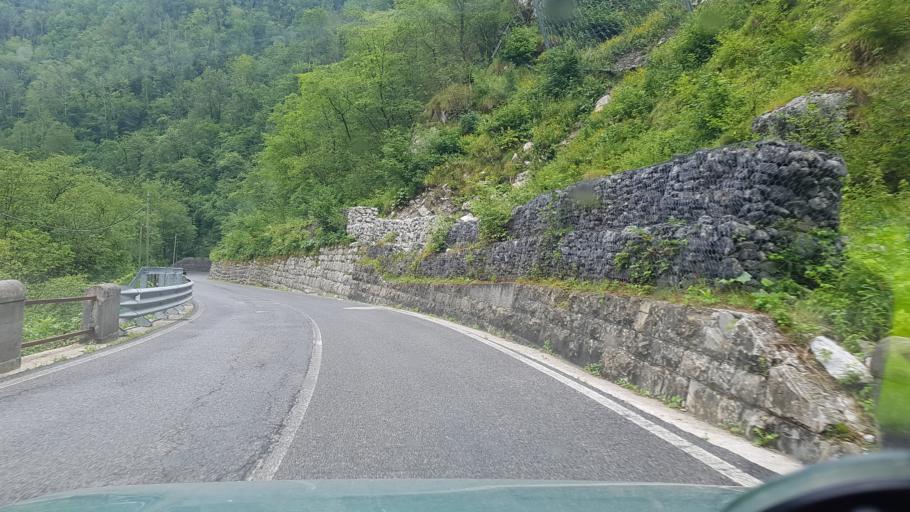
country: IT
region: Friuli Venezia Giulia
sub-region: Provincia di Udine
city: Lusevera
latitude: 46.2517
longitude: 13.2537
